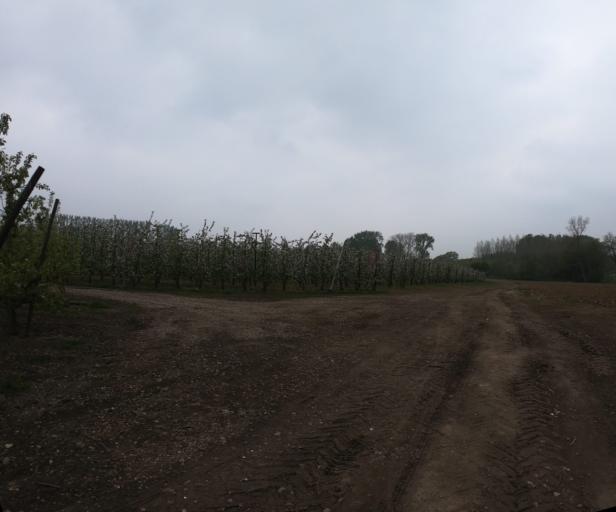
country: BE
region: Flanders
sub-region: Provincie Vlaams-Brabant
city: Gooik
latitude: 50.7577
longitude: 4.1144
